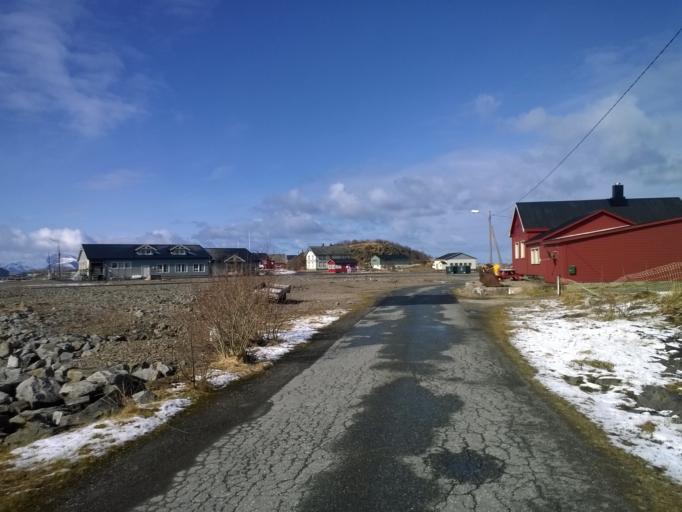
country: NO
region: Nordland
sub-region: Vagan
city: Kabelvag
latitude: 68.3875
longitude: 14.4197
